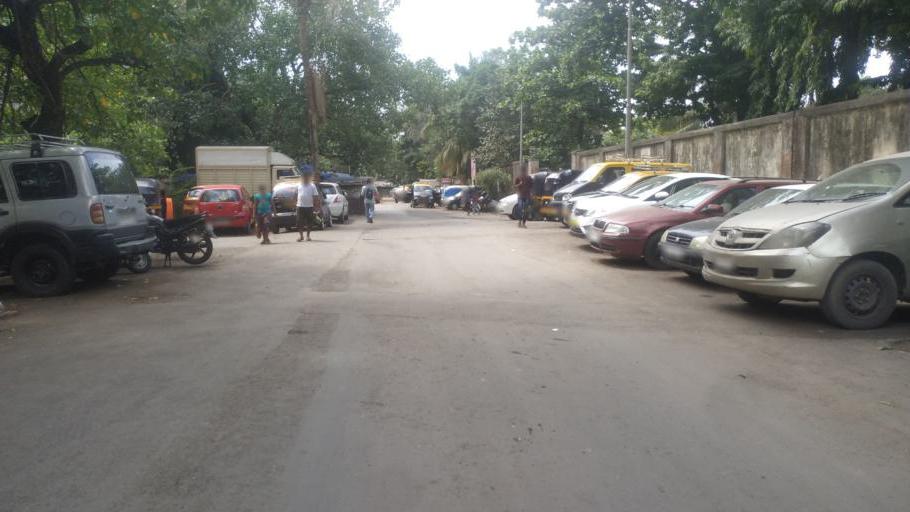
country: IN
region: Maharashtra
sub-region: Mumbai Suburban
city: Mumbai
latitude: 19.0444
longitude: 72.8752
